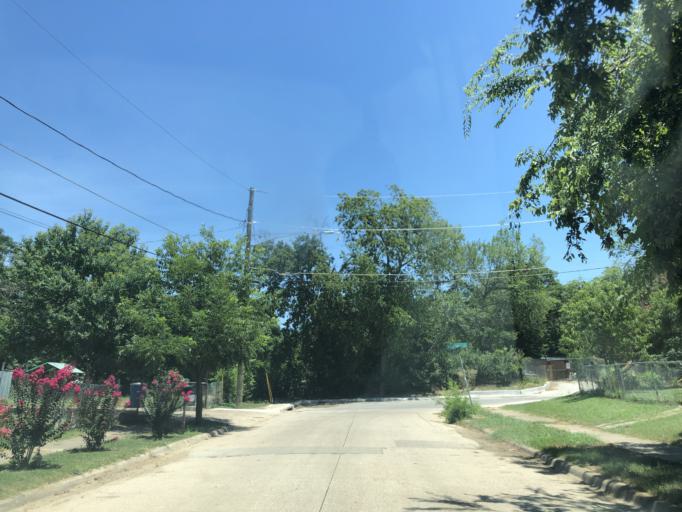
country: US
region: Texas
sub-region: Dallas County
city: Irving
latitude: 32.7936
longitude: -96.9030
